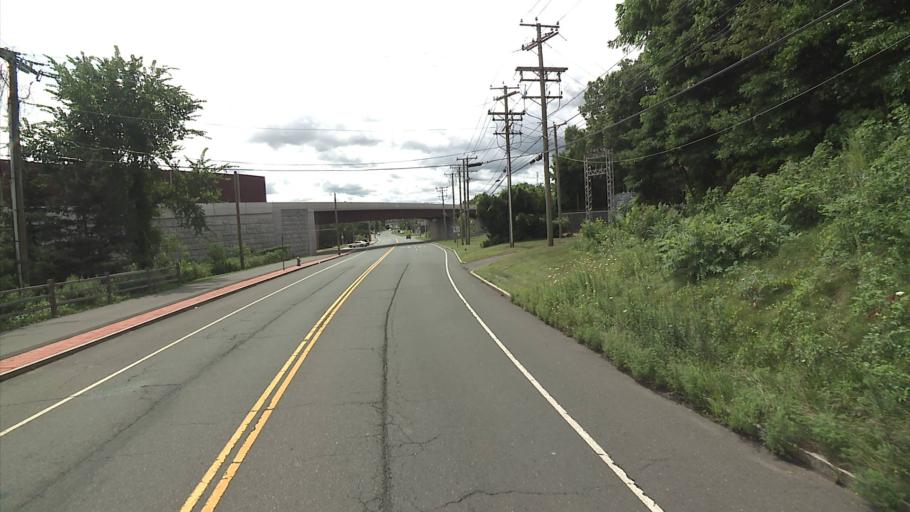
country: US
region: Connecticut
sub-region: Hartford County
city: New Britain
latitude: 41.6861
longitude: -72.7607
